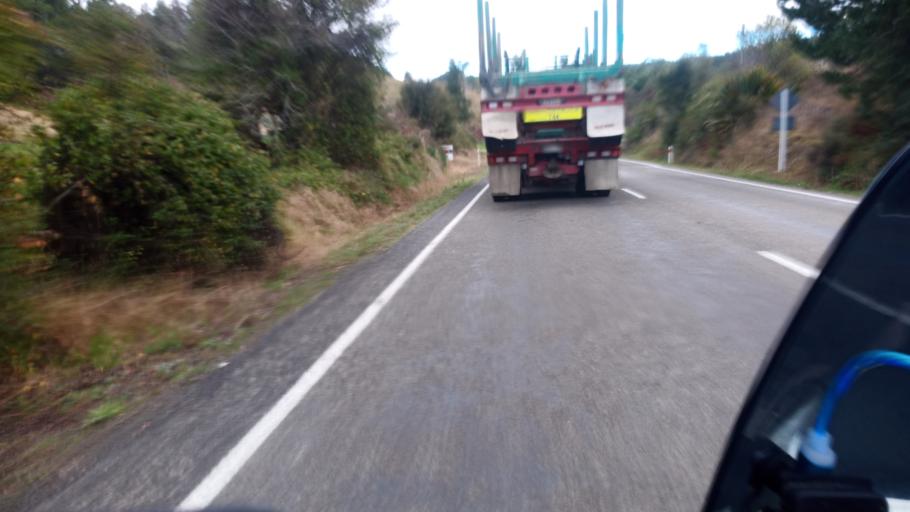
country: NZ
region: Gisborne
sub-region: Gisborne District
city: Gisborne
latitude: -38.0511
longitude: 178.2997
